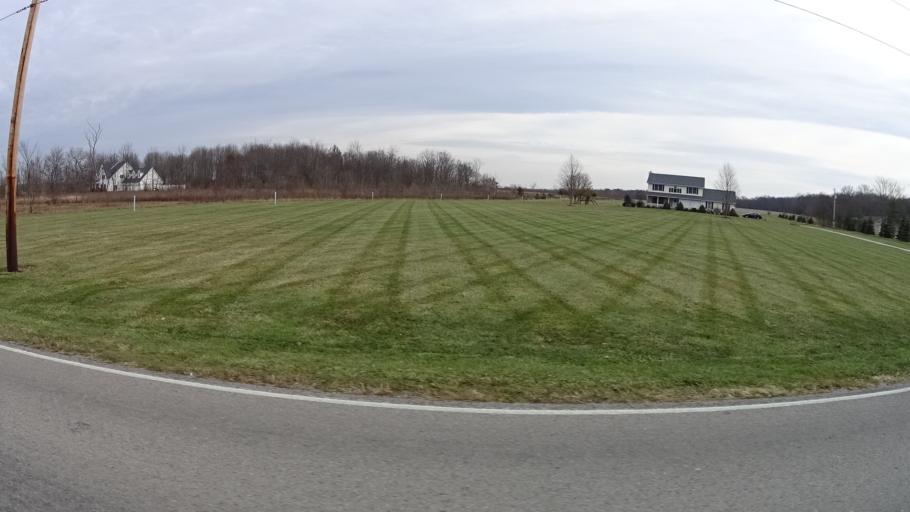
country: US
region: Ohio
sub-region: Lorain County
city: Lagrange
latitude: 41.1607
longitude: -82.0916
